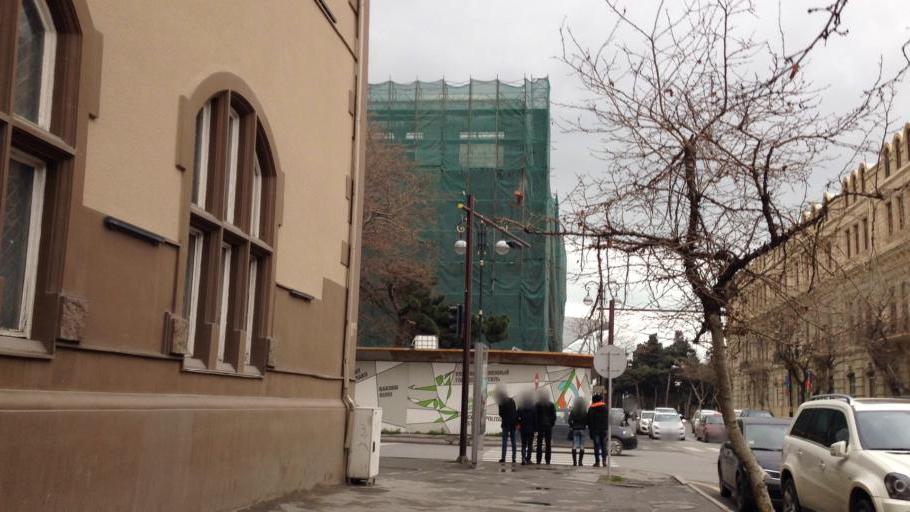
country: AZ
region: Baki
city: Baku
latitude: 40.3726
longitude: 49.8477
